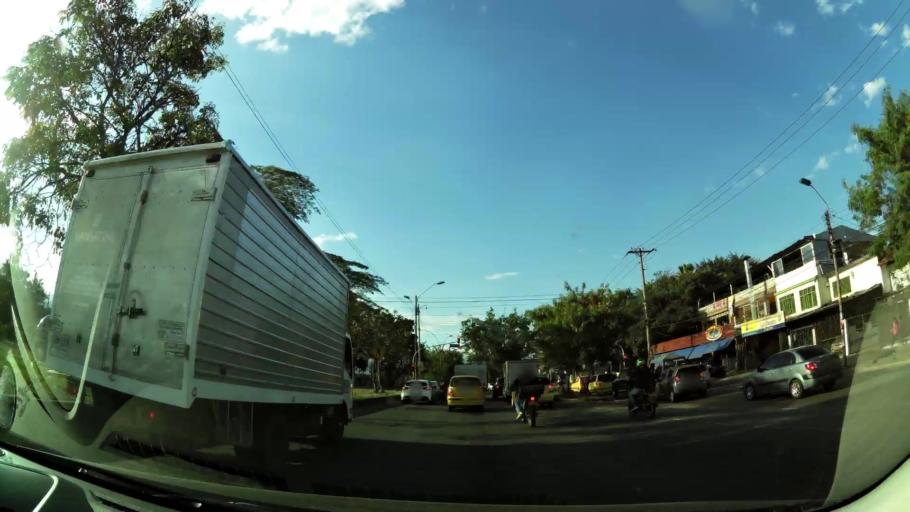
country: CO
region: Valle del Cauca
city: Cali
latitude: 3.4760
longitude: -76.4874
